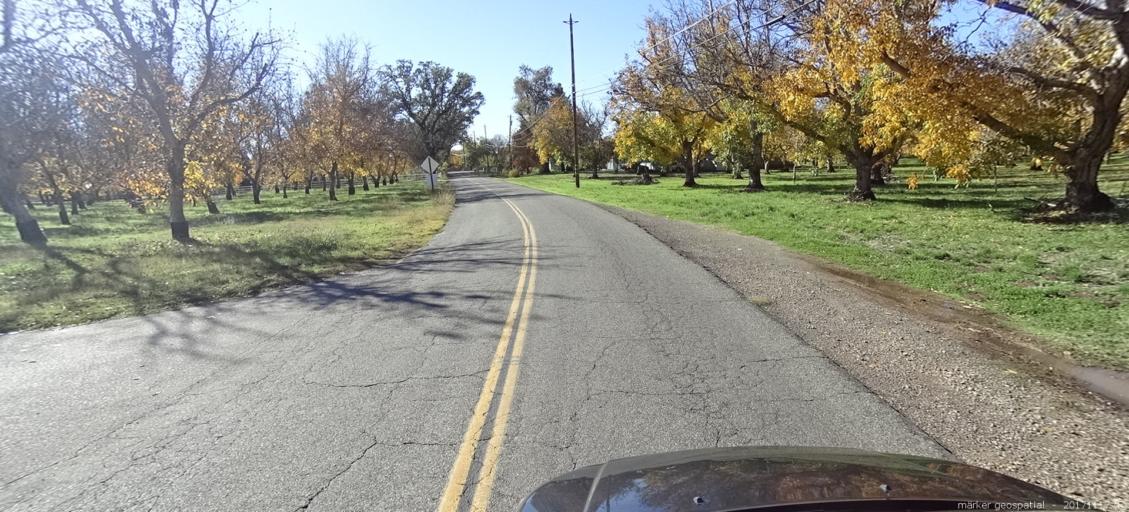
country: US
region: California
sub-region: Shasta County
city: Anderson
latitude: 40.4463
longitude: -122.2502
